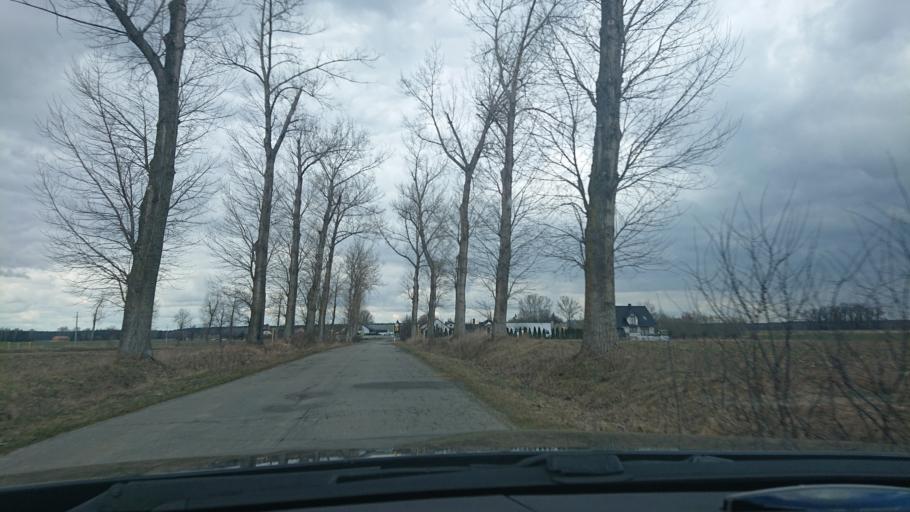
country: PL
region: Greater Poland Voivodeship
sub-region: Powiat gnieznienski
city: Niechanowo
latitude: 52.5867
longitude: 17.6997
